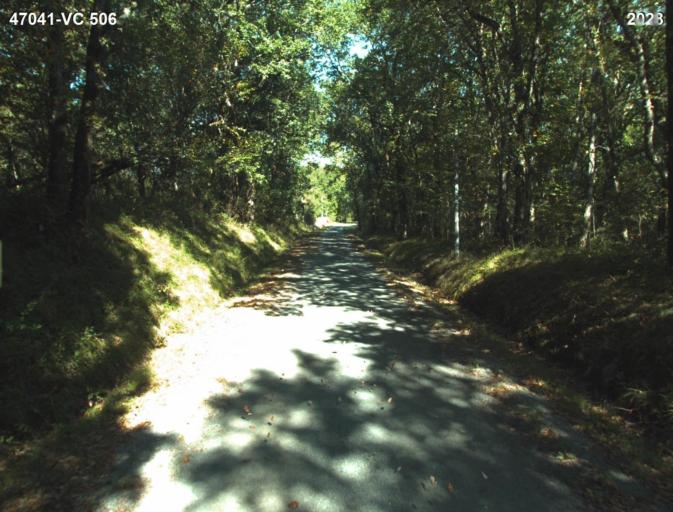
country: FR
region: Aquitaine
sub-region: Departement du Lot-et-Garonne
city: Port-Sainte-Marie
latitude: 44.1987
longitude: 0.3856
